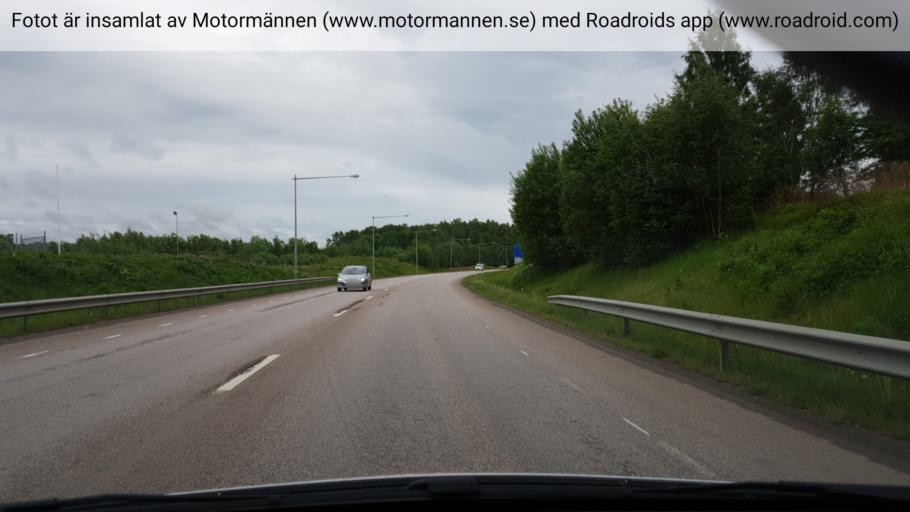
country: SE
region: Vaestra Goetaland
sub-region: Skovde Kommun
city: Skoevde
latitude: 58.3858
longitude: 13.8749
